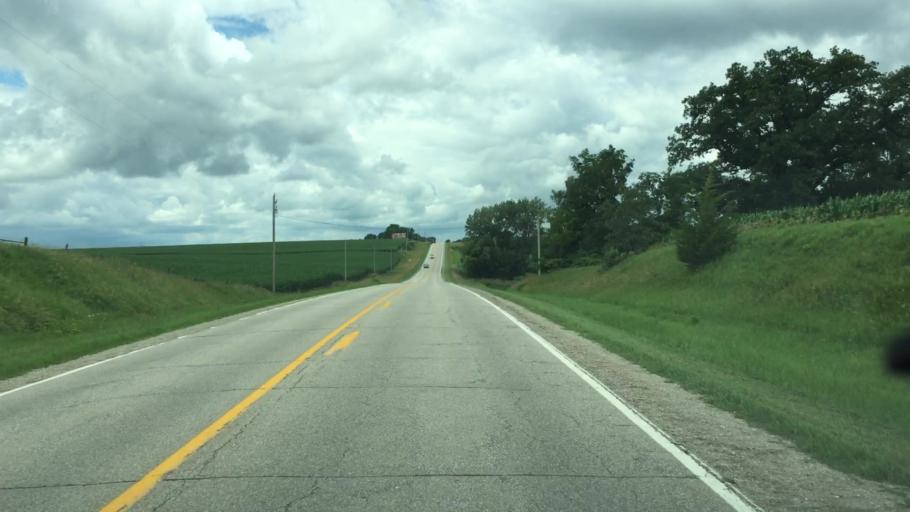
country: US
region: Iowa
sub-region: Jasper County
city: Monroe
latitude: 41.5735
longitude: -93.0628
